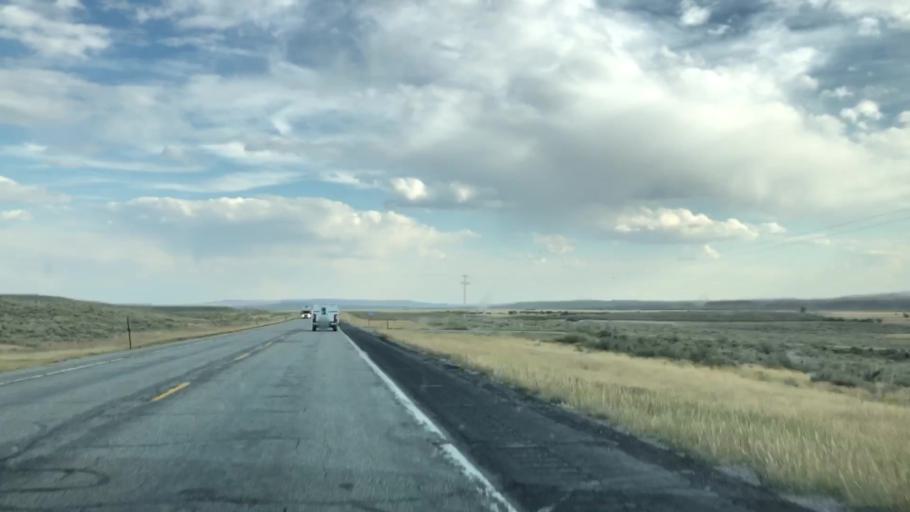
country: US
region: Wyoming
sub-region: Sublette County
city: Pinedale
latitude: 43.0526
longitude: -110.1528
